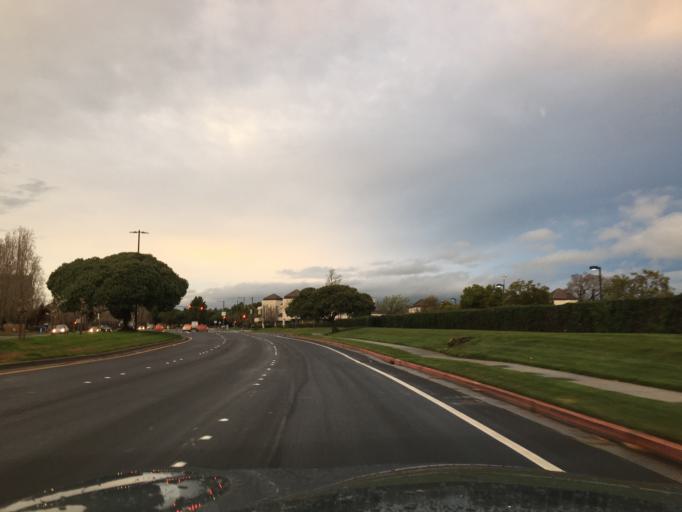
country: US
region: California
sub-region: San Mateo County
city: Redwood Shores
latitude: 37.5200
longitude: -122.2521
